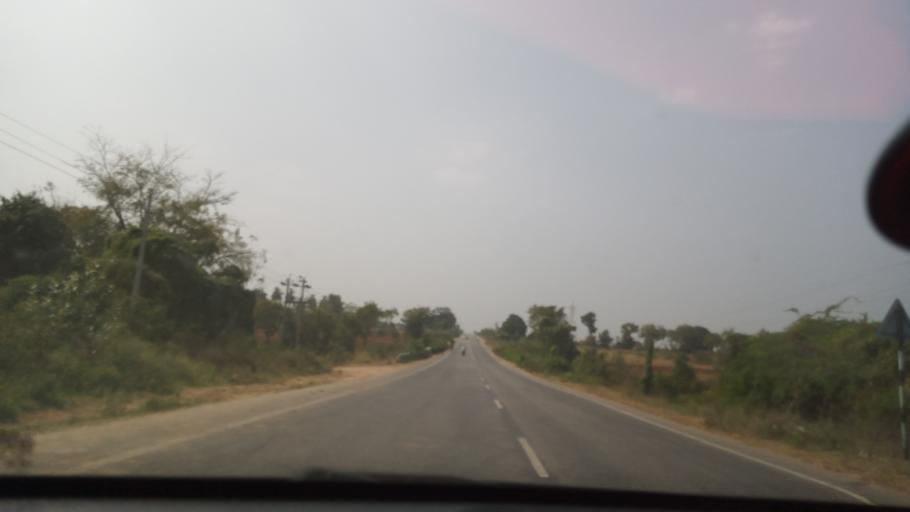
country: IN
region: Karnataka
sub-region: Chamrajnagar
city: Chamrajnagar
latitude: 11.9980
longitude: 76.8480
